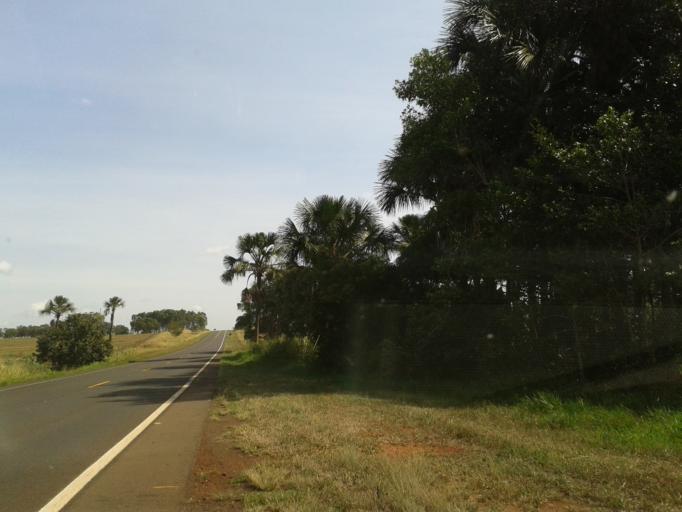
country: BR
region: Minas Gerais
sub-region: Campina Verde
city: Campina Verde
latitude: -19.5231
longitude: -49.5682
